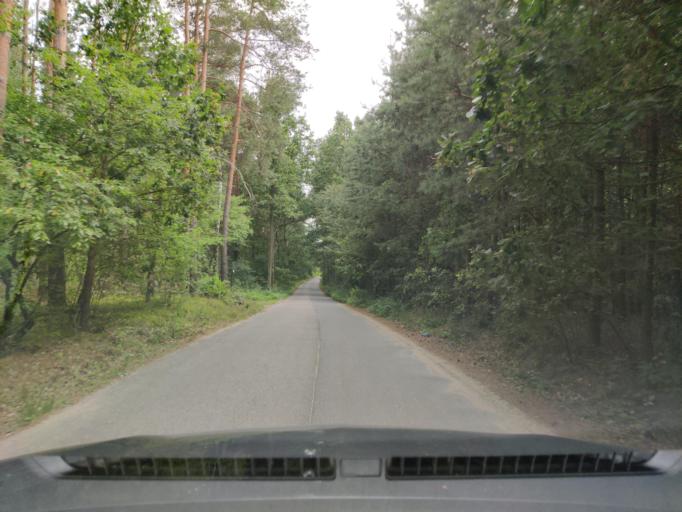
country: PL
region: Masovian Voivodeship
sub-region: Powiat pultuski
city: Pultusk
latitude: 52.7370
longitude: 21.1381
